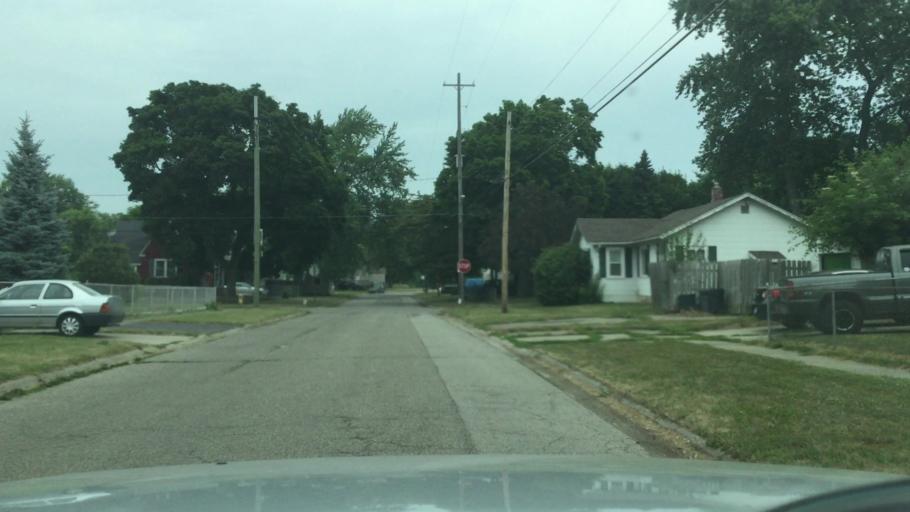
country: US
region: Michigan
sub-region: Genesee County
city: Flint
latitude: 42.9904
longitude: -83.6858
